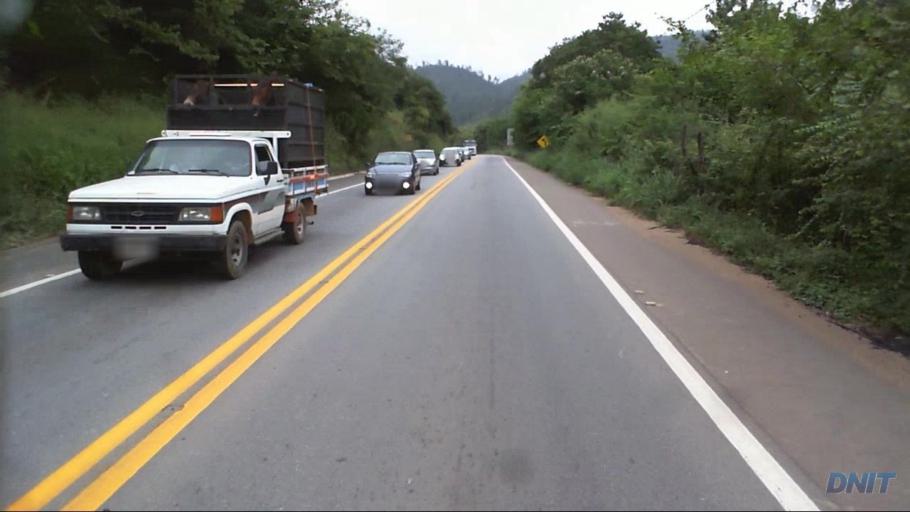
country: BR
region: Minas Gerais
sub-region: Timoteo
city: Timoteo
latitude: -19.5489
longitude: -42.6987
